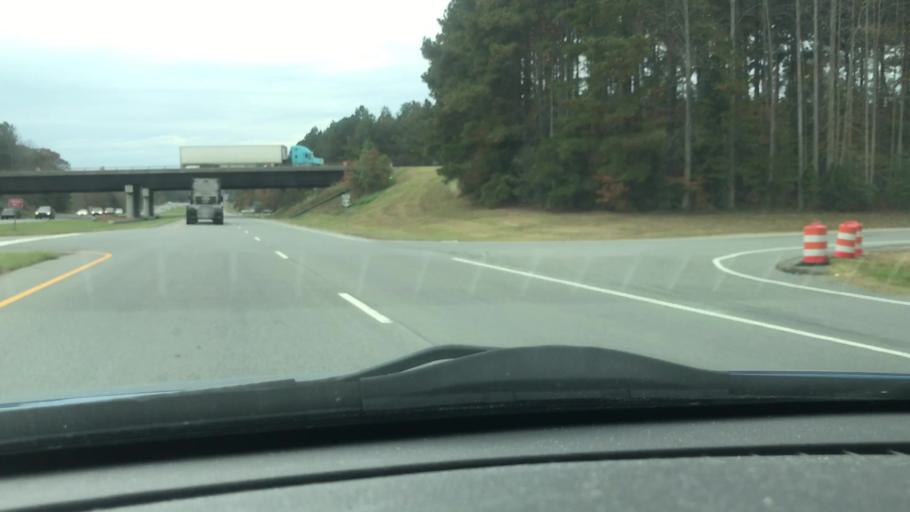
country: US
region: North Carolina
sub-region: Davidson County
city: Lexington
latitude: 35.8092
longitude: -80.1805
